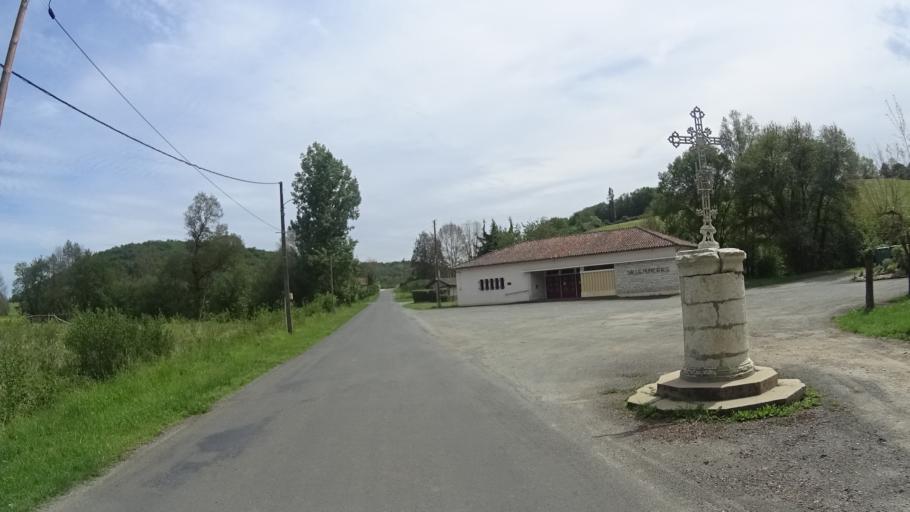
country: FR
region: Aquitaine
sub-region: Departement de la Dordogne
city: Sourzac
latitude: 45.0139
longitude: 0.4519
